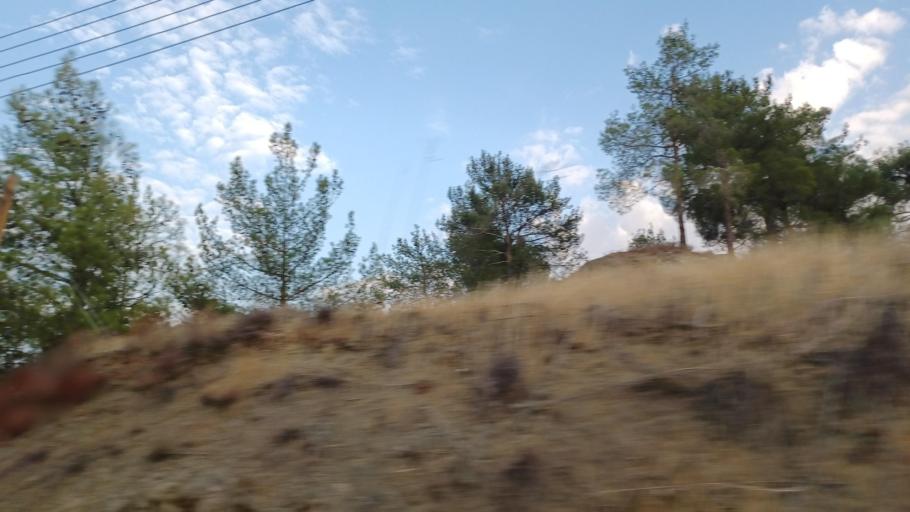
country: CY
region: Limassol
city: Pelendri
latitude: 34.8510
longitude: 32.9508
